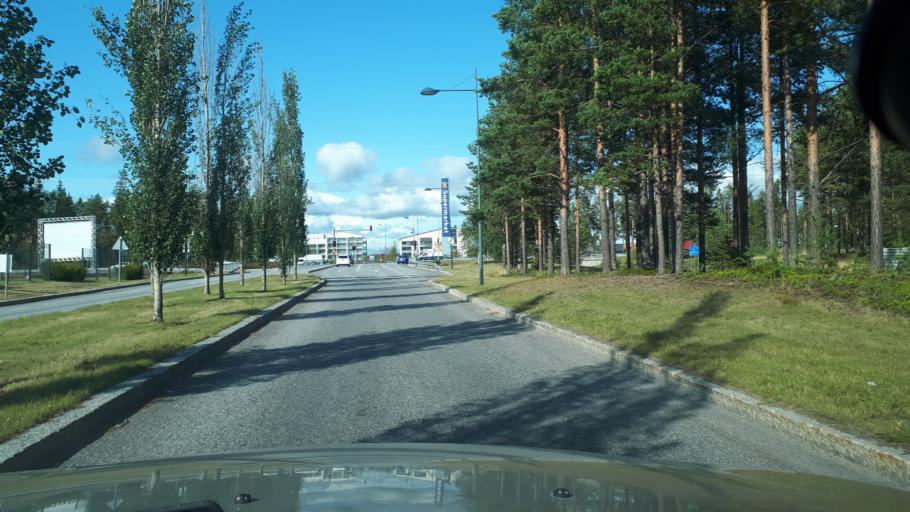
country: FI
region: Northern Ostrobothnia
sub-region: Oulu
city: Oulu
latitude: 65.0773
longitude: 25.4516
